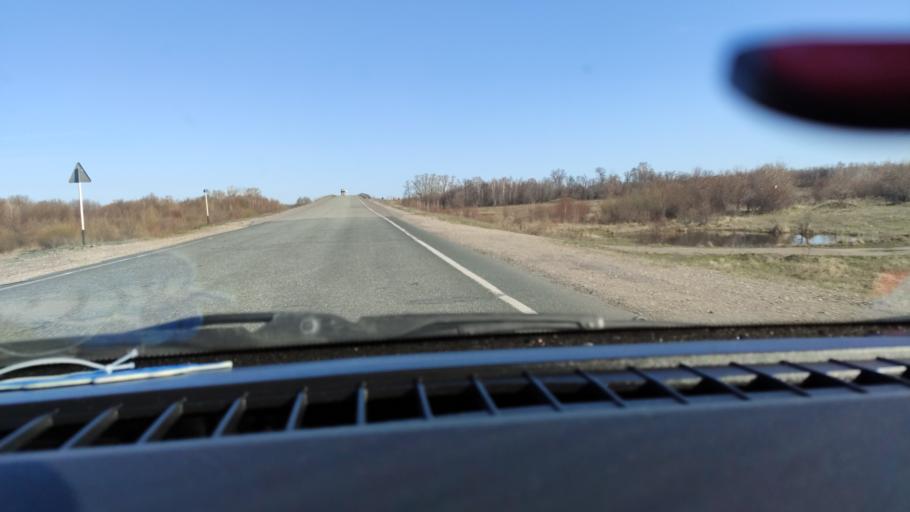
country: RU
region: Samara
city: Varlamovo
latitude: 53.1613
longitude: 48.2827
